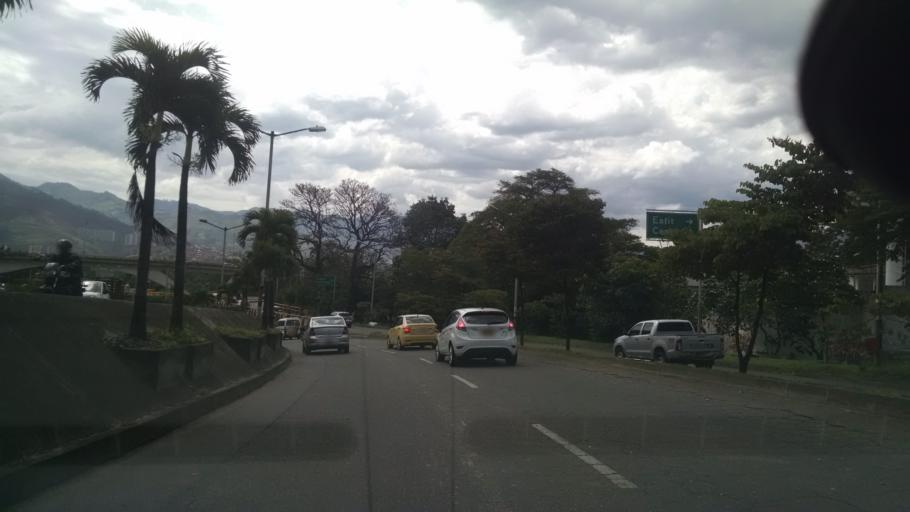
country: CO
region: Antioquia
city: Envigado
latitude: 6.1943
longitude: -75.5777
